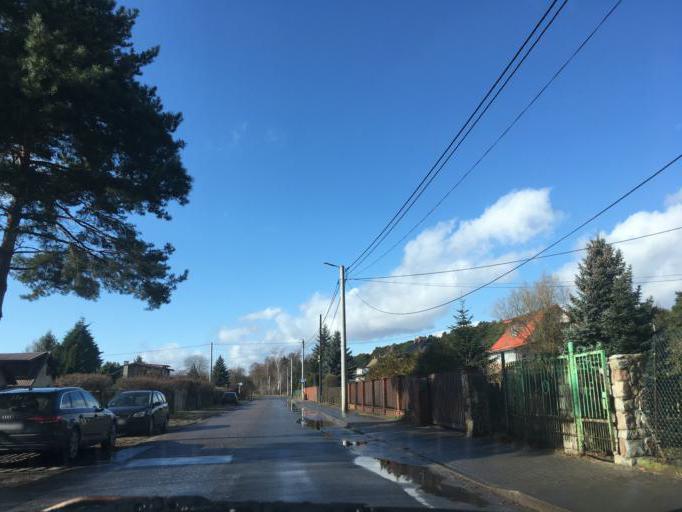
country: PL
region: Pomeranian Voivodeship
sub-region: Powiat gdanski
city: Cedry Wielkie
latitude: 54.3488
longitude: 18.8052
